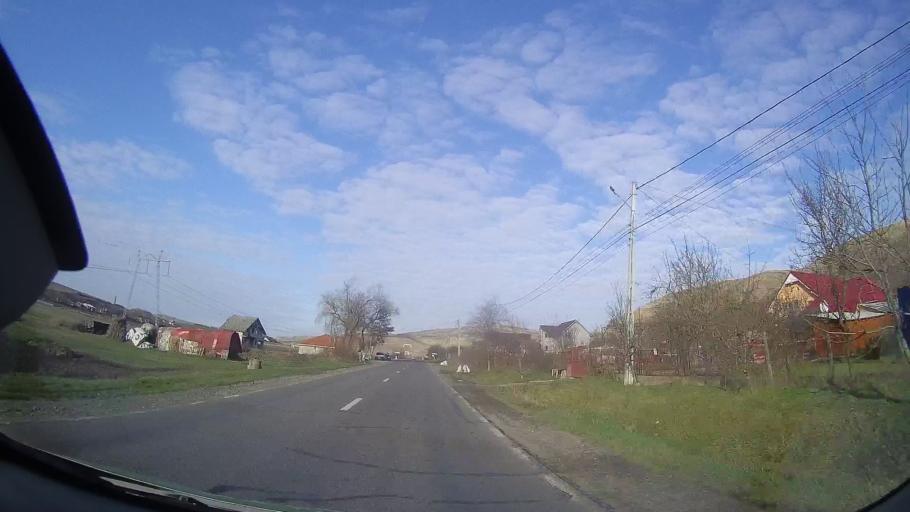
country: RO
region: Cluj
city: Caianu Mic
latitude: 46.8058
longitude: 23.8735
